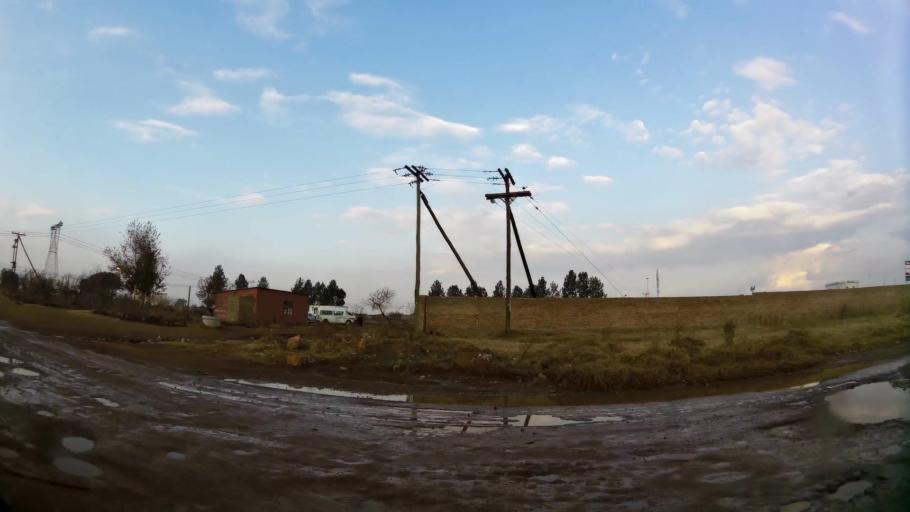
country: ZA
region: Gauteng
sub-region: City of Johannesburg Metropolitan Municipality
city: Orange Farm
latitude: -26.5544
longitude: 27.8304
